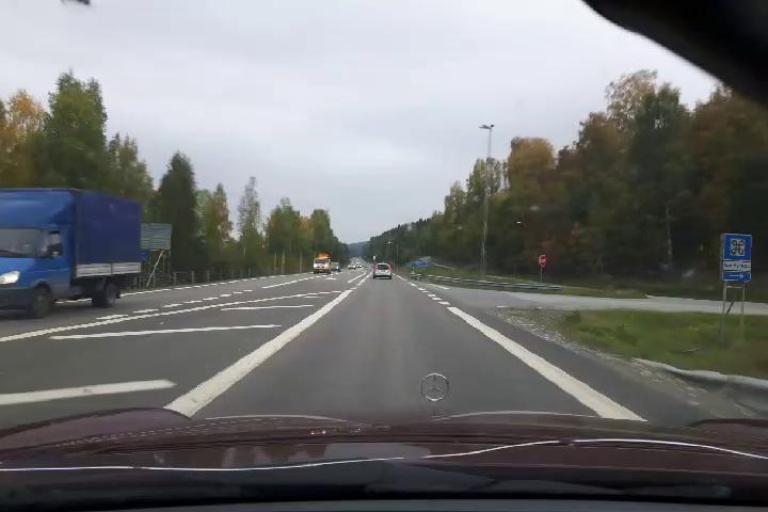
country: SE
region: Vaesternorrland
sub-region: Kramfors Kommun
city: Nordingra
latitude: 63.0450
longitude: 18.3260
